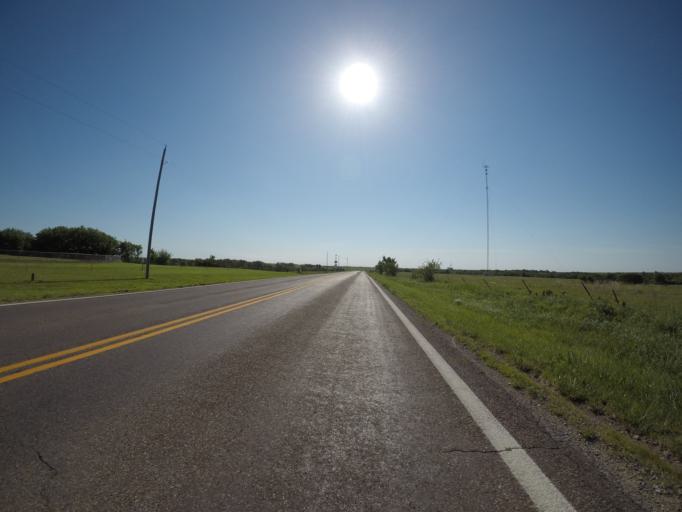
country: US
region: Kansas
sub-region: Lyon County
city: Emporia
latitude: 38.6588
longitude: -96.1476
